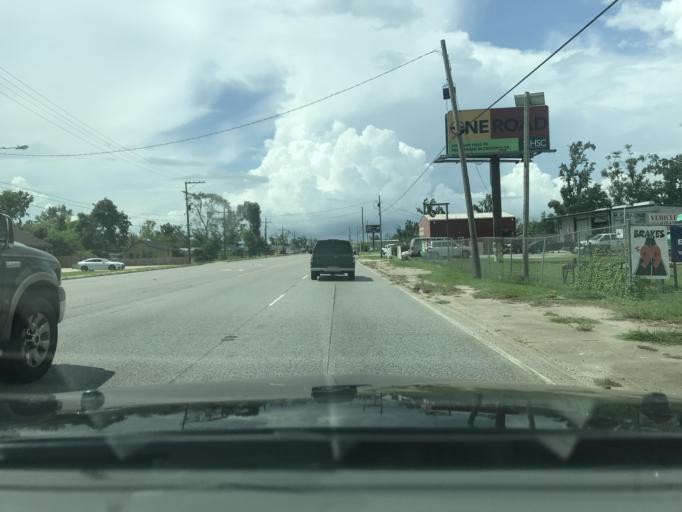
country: US
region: Louisiana
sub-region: Calcasieu Parish
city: Moss Bluff
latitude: 30.2623
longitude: -93.1807
